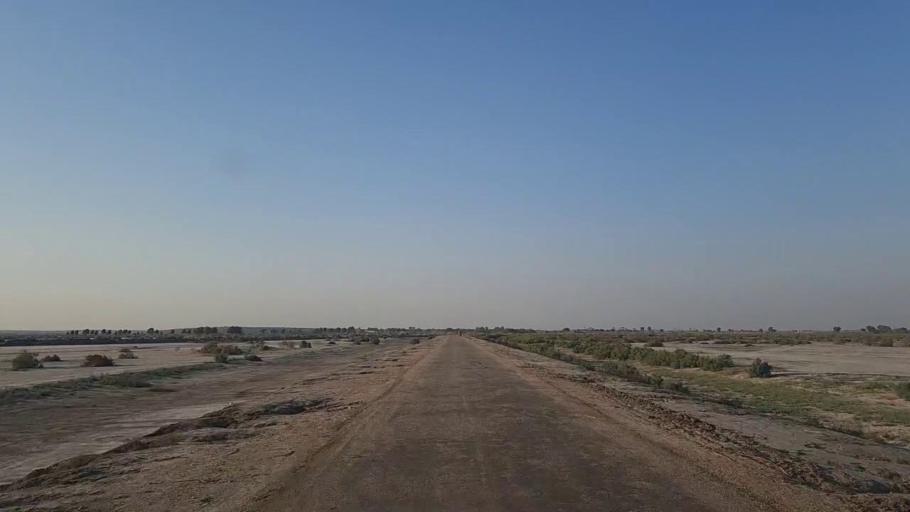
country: PK
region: Sindh
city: Jam Sahib
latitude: 26.3242
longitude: 68.6676
